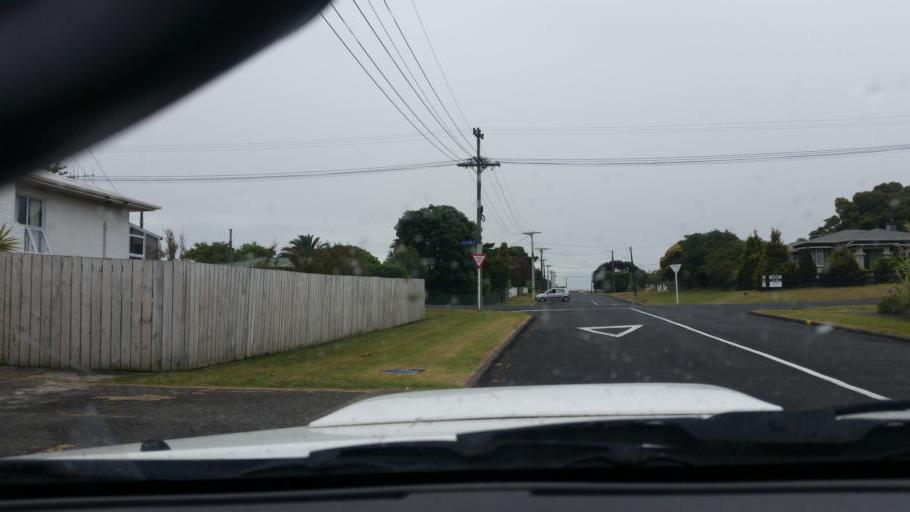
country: NZ
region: Northland
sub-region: Kaipara District
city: Dargaville
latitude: -35.9357
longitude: 173.8696
